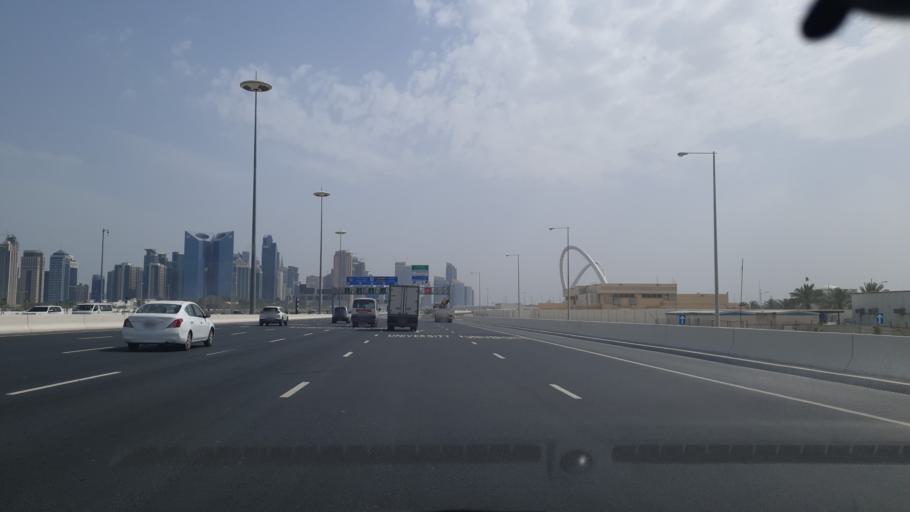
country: QA
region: Baladiyat ad Dawhah
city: Doha
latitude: 25.3445
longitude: 51.5202
